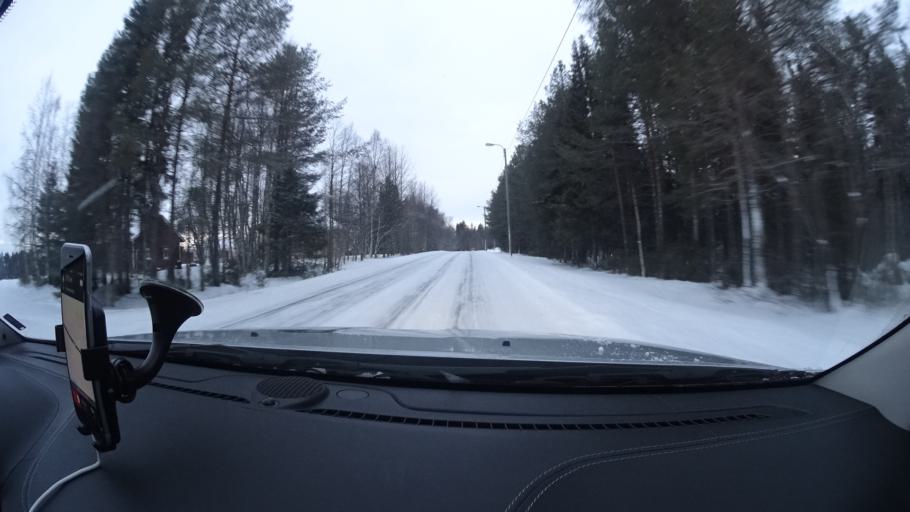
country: FI
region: Northern Ostrobothnia
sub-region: Koillismaa
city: Kuusamo
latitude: 66.0965
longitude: 28.6986
